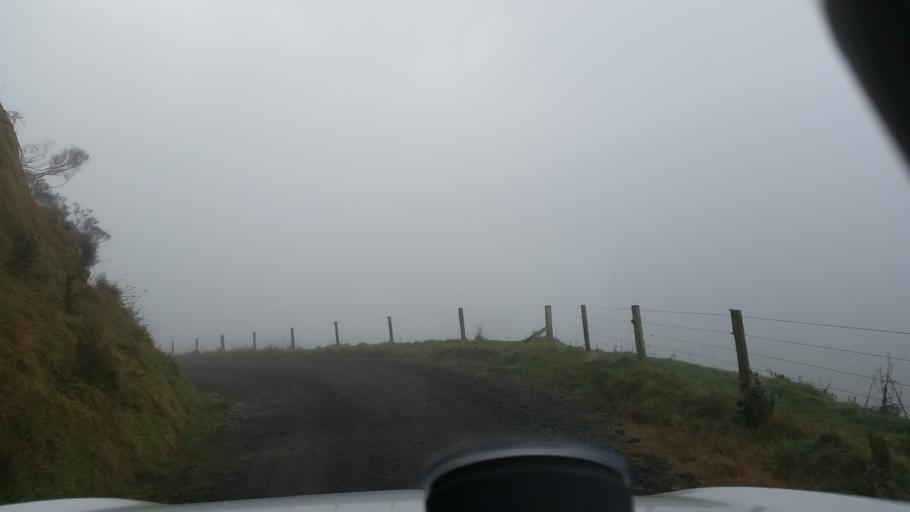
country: NZ
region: Taranaki
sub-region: South Taranaki District
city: Eltham
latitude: -39.4099
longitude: 174.4292
